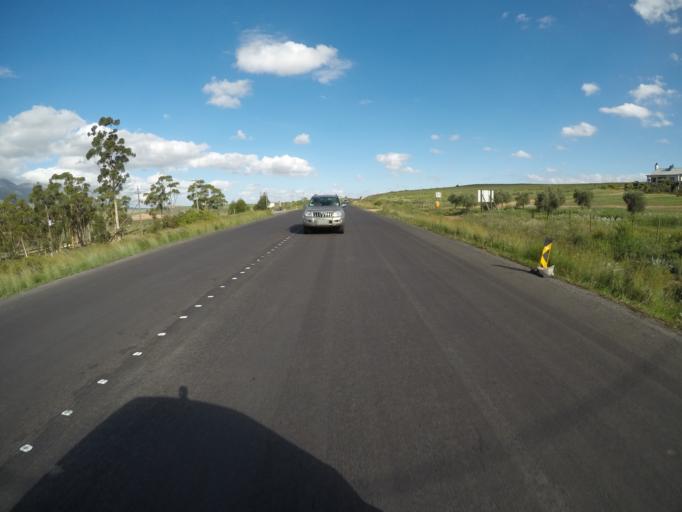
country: ZA
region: Western Cape
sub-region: Cape Winelands District Municipality
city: Ashton
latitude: -33.9390
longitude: 20.2141
